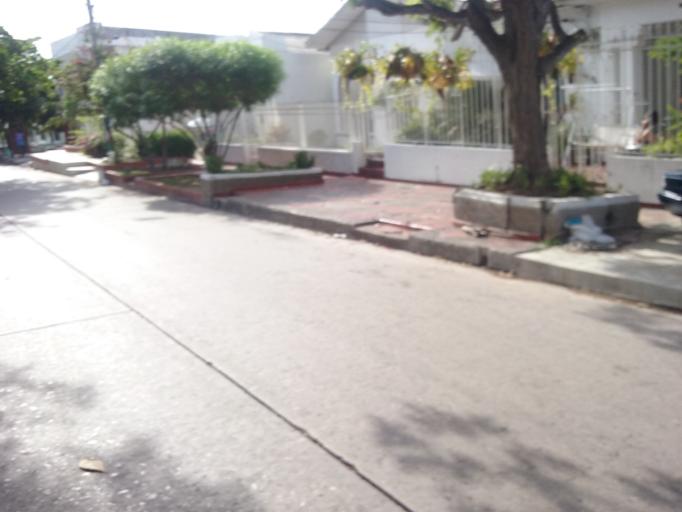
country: CO
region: Atlantico
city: Barranquilla
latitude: 10.9826
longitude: -74.7946
